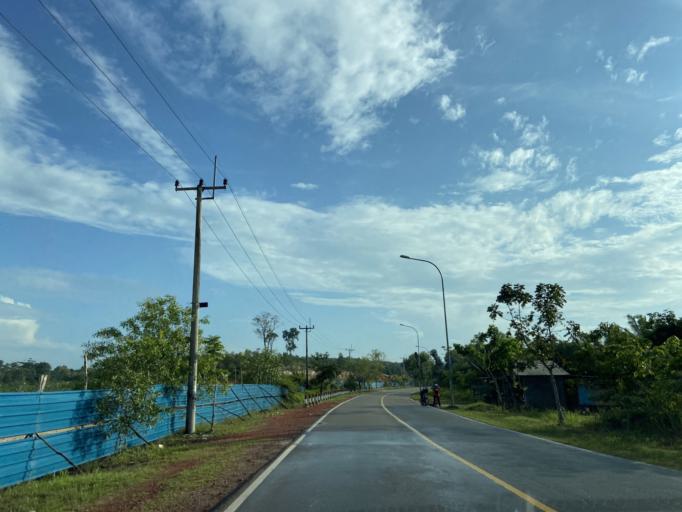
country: SG
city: Singapore
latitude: 0.9556
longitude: 104.0528
